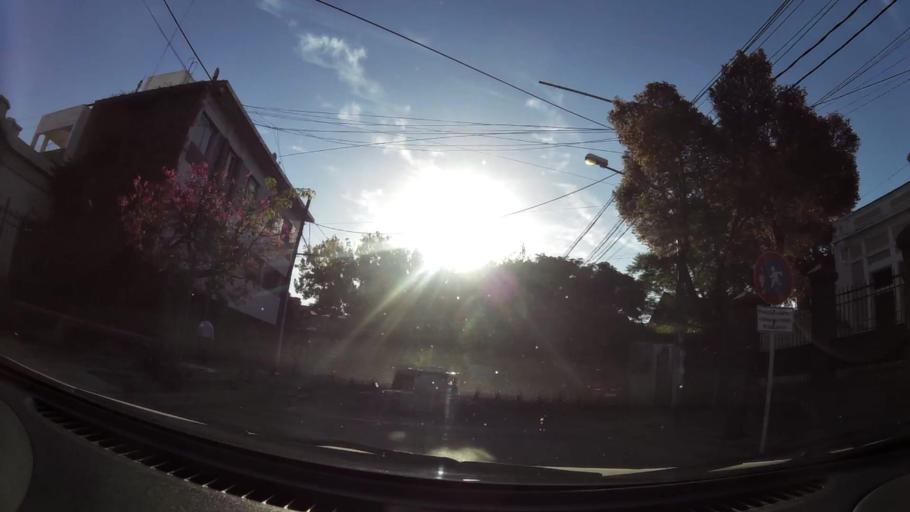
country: AR
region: Mendoza
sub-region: Departamento de Godoy Cruz
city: Godoy Cruz
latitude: -32.9078
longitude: -68.8483
